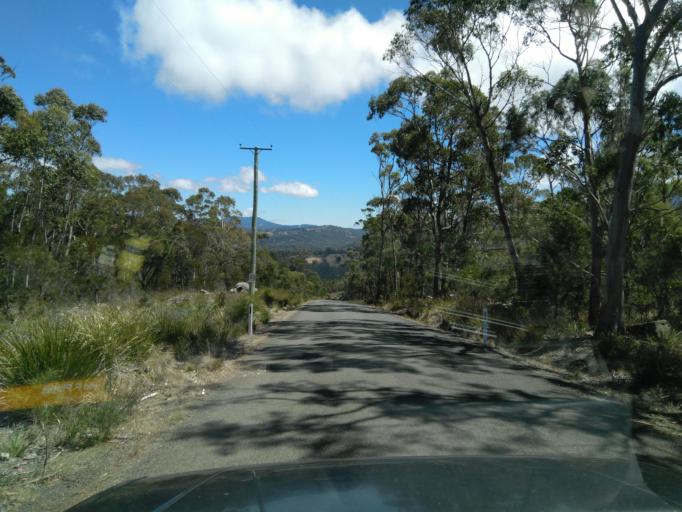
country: AU
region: Tasmania
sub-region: Kingborough
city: Taroona
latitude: -42.9497
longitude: 147.3260
